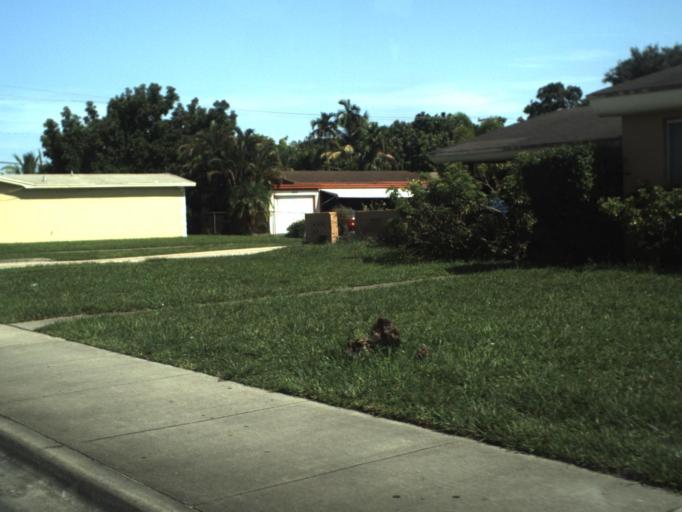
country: US
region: Florida
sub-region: Miami-Dade County
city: Norland
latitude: 25.9423
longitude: -80.2095
